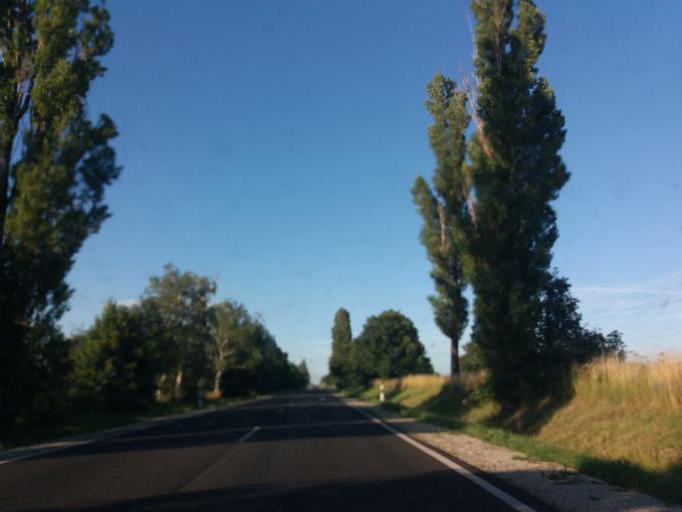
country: HU
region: Fejer
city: Baracska
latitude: 47.2693
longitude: 18.7309
